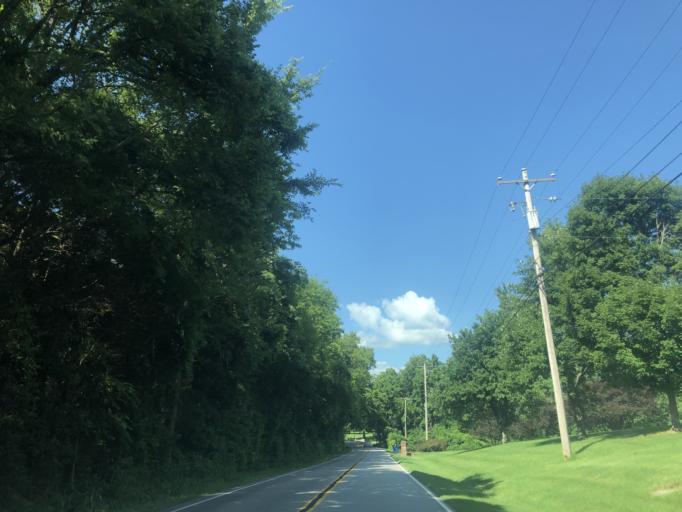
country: US
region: Tennessee
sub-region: Wilson County
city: Green Hill
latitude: 36.1952
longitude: -86.5990
